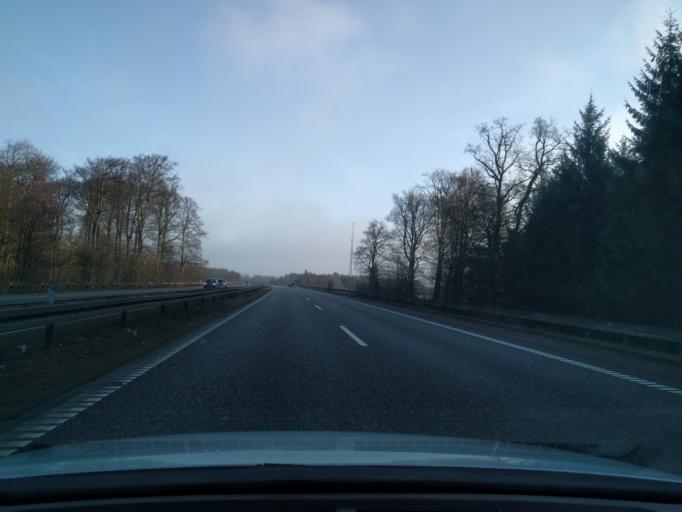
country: DK
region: Zealand
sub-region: Soro Kommune
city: Soro
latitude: 55.4368
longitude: 11.4924
